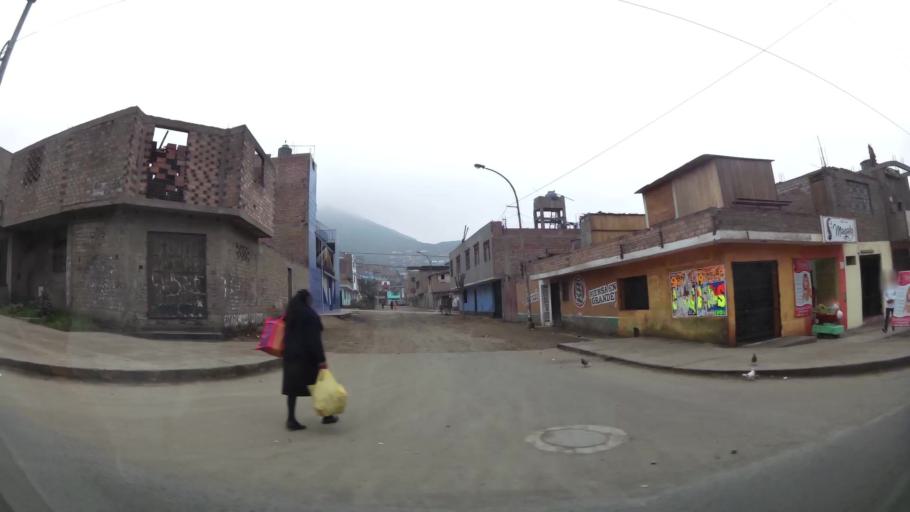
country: PE
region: Lima
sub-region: Lima
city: Urb. Santo Domingo
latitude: -11.9132
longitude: -77.0239
